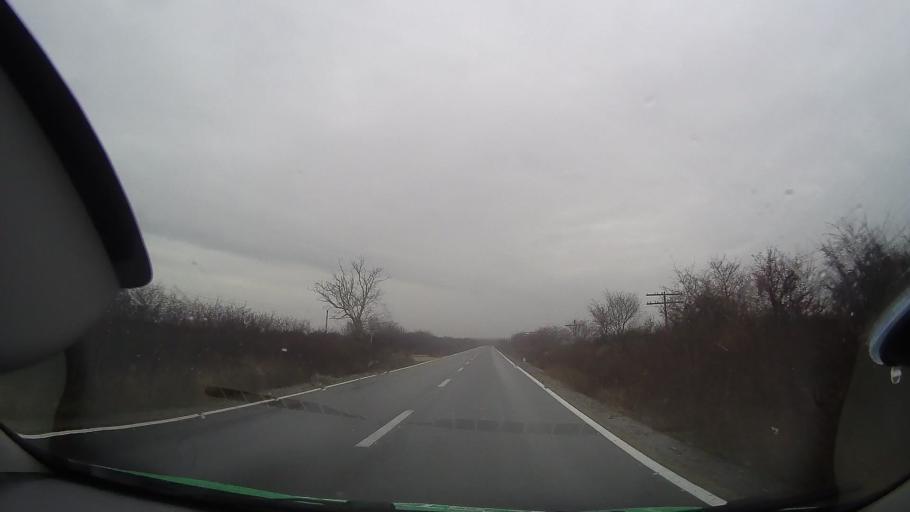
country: RO
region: Bihor
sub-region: Comuna Olcea
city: Calacea
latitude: 46.7208
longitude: 21.9502
